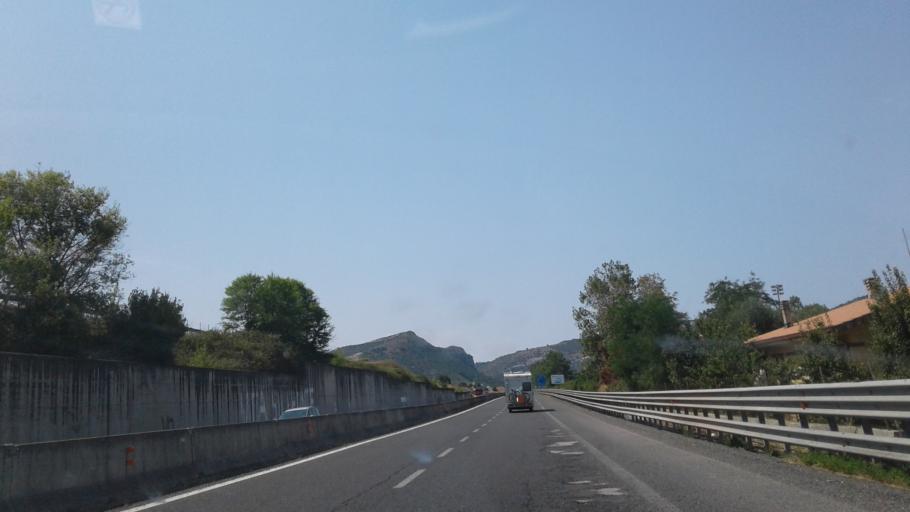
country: IT
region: Sardinia
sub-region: Provincia di Sassari
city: Muros
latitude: 40.6807
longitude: 8.6389
